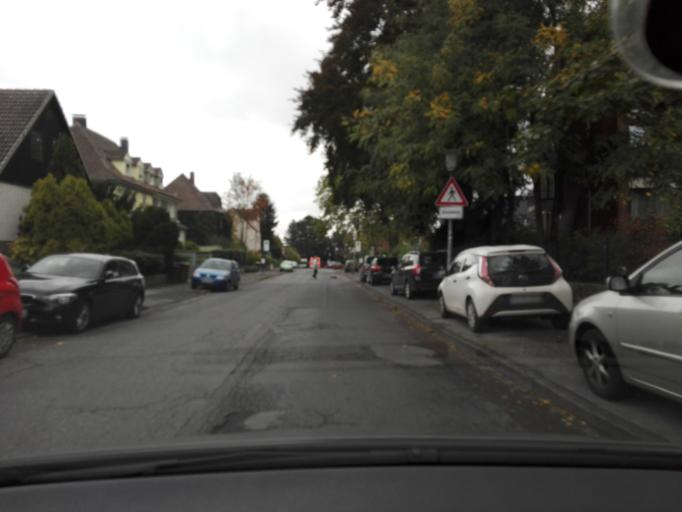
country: DE
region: North Rhine-Westphalia
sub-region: Regierungsbezirk Arnsberg
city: Unna
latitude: 51.5353
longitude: 7.6765
